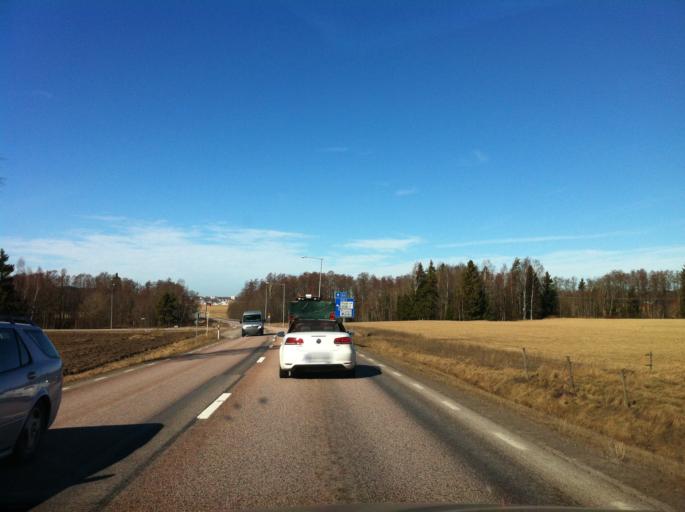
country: SE
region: Vaestra Goetaland
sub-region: Gullspangs Kommun
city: Hova
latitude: 58.9063
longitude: 14.1180
